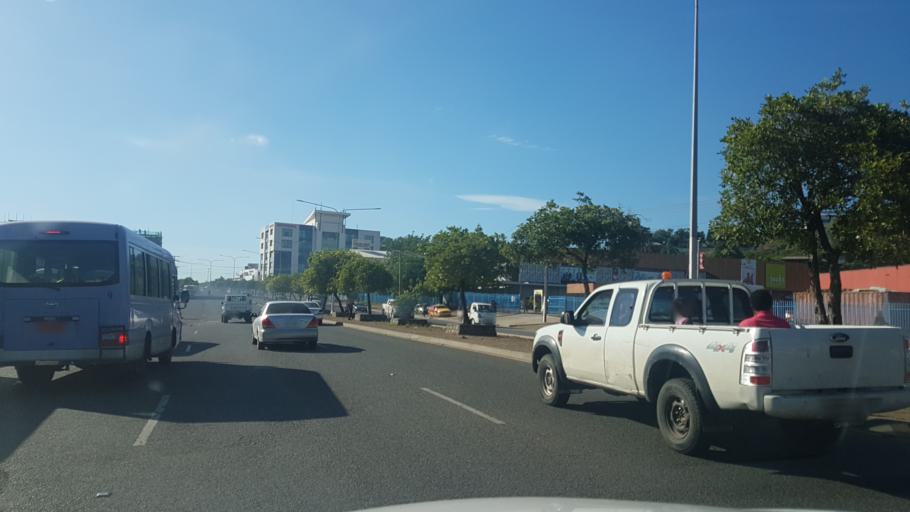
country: PG
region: National Capital
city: Port Moresby
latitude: -9.4528
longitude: 147.1876
